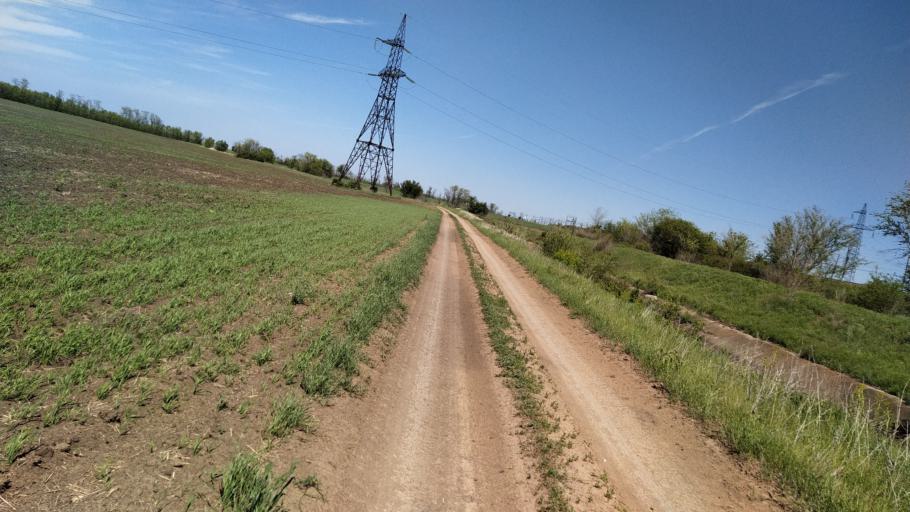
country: RU
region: Rostov
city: Kuleshovka
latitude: 47.0395
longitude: 39.6425
